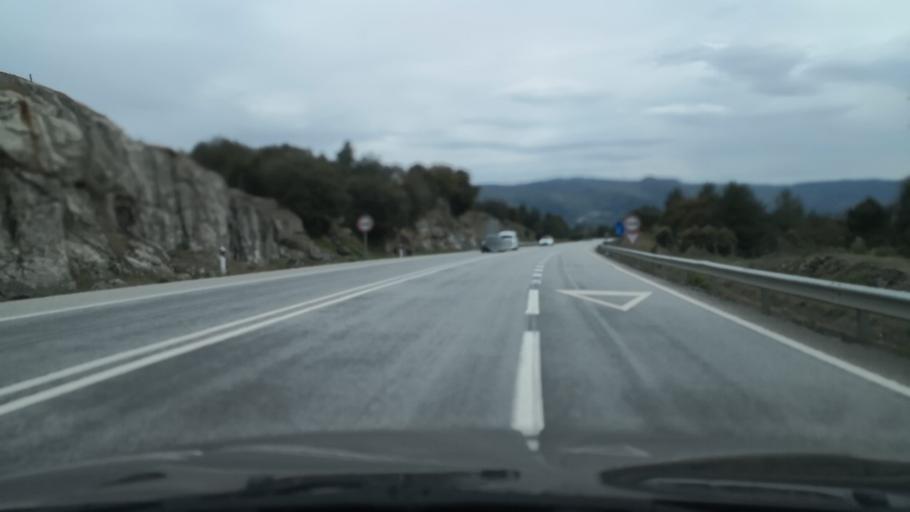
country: PT
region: Guarda
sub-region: Celorico da Beira
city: Celorico da Beira
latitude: 40.6287
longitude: -7.3083
